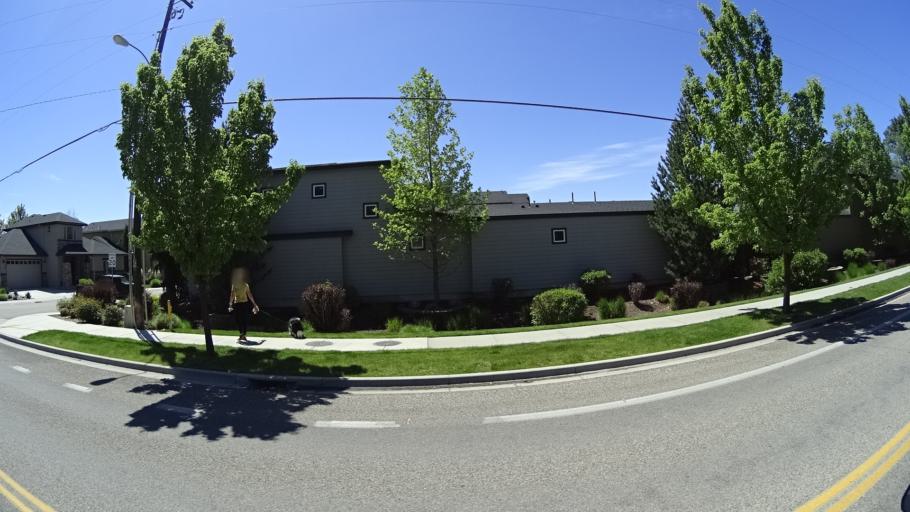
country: US
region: Idaho
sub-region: Ada County
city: Boise
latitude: 43.5861
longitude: -116.1790
